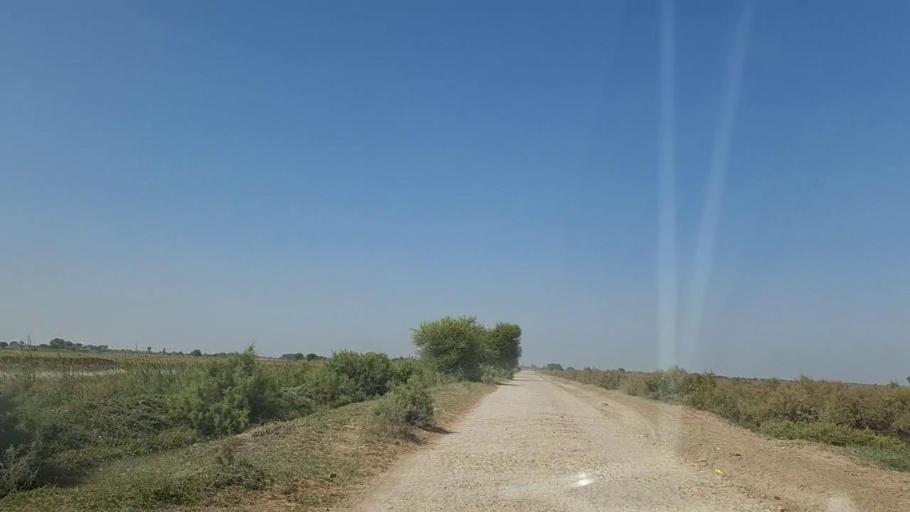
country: PK
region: Sindh
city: Chuhar Jamali
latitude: 24.4215
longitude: 68.0131
